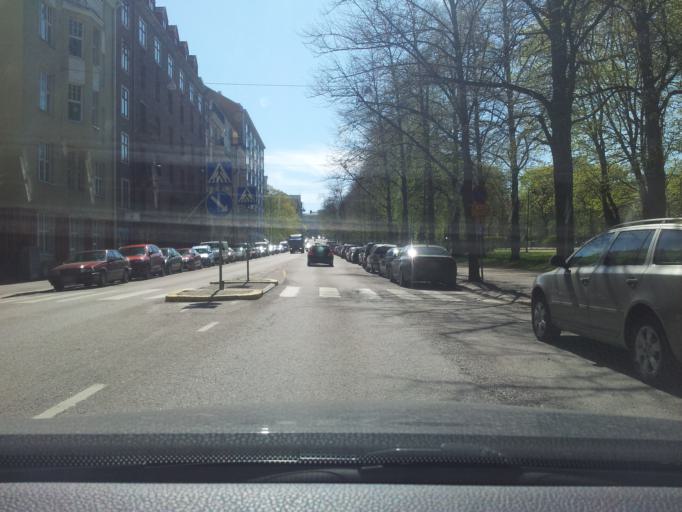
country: FI
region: Uusimaa
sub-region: Helsinki
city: Helsinki
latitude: 60.1829
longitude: 24.9192
